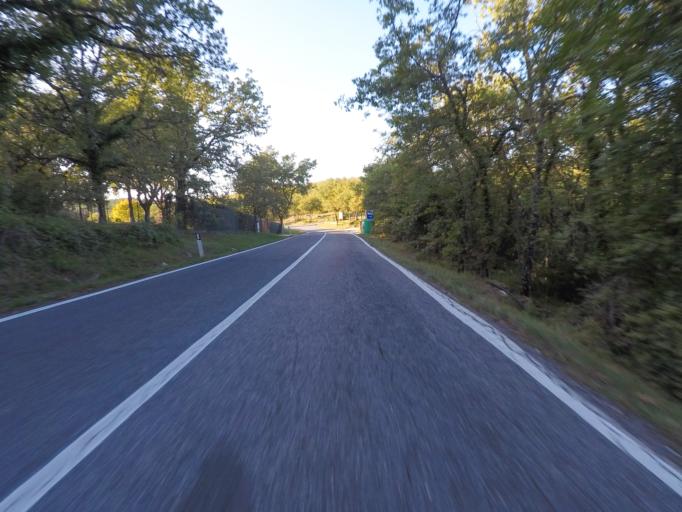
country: IT
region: Tuscany
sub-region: Provincia di Siena
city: Castellina in Chianti
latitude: 43.4834
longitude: 11.3254
